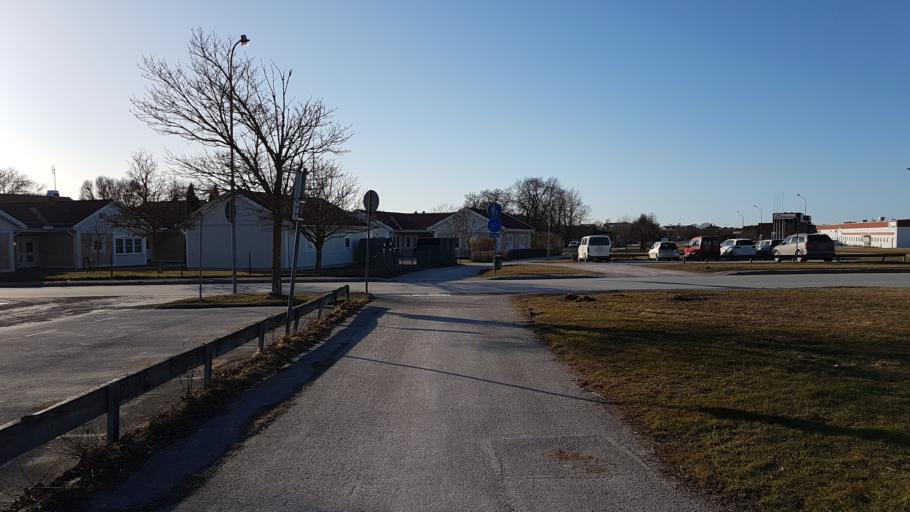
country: SE
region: Gotland
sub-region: Gotland
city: Visby
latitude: 57.6413
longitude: 18.3200
